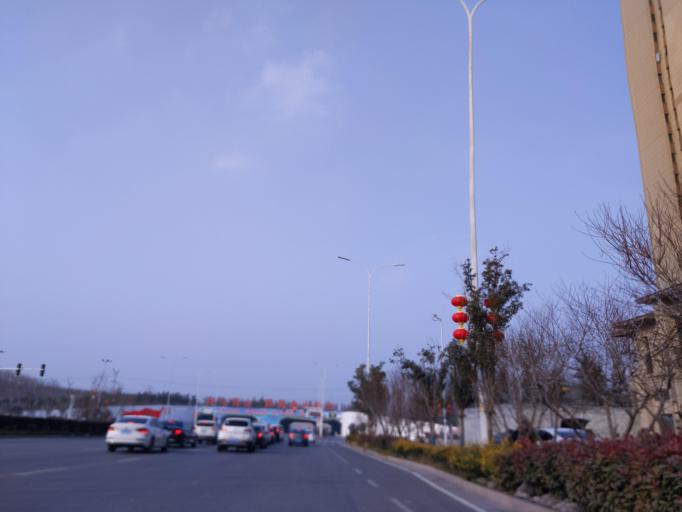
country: CN
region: Henan Sheng
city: Puyang
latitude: 35.8164
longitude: 115.0226
